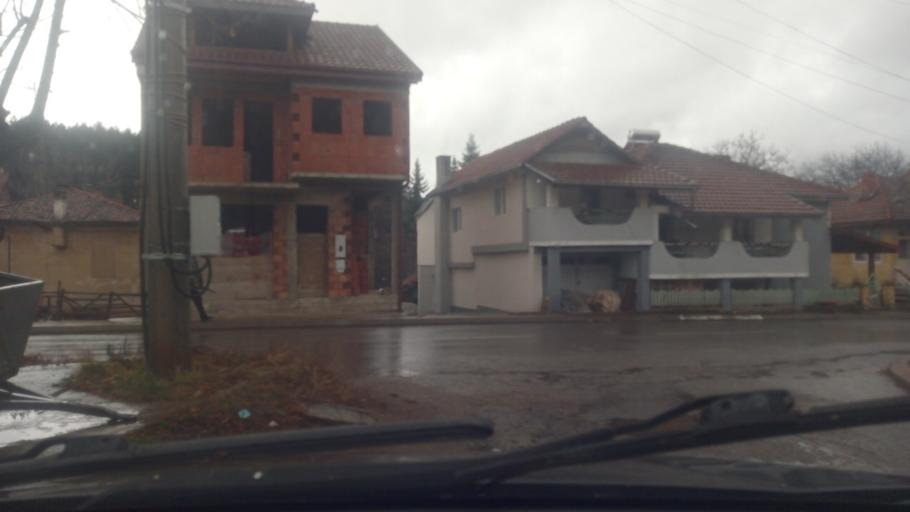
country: MK
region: Pehcevo
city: Pehcevo
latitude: 41.7621
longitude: 22.8855
